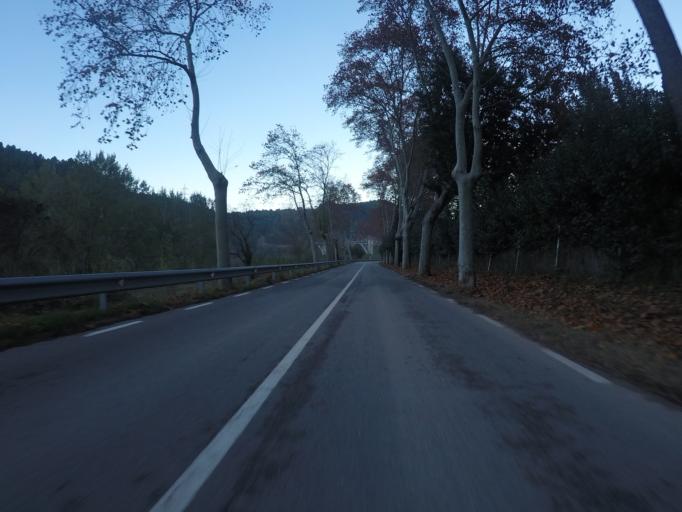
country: ES
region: Catalonia
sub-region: Provincia de Barcelona
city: Monistrol de Montserrat
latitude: 41.6186
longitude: 1.8530
